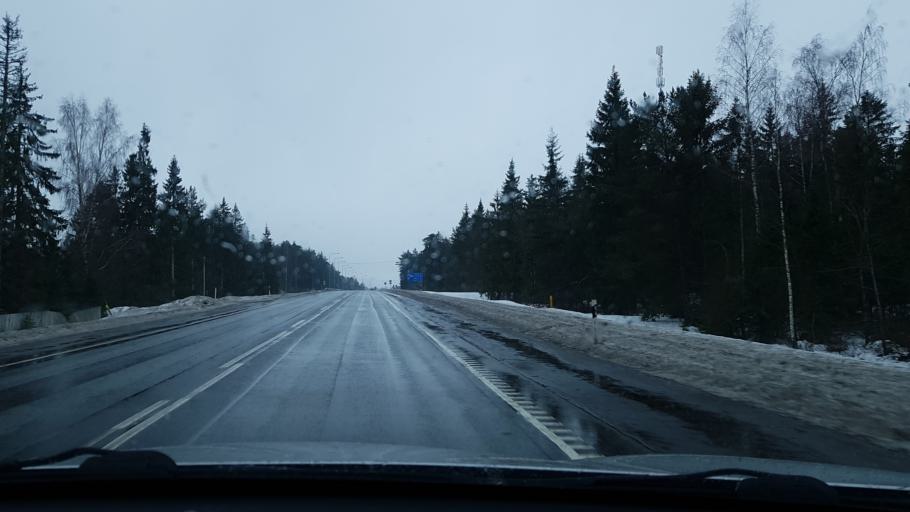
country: EE
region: Raplamaa
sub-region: Kohila vald
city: Kohila
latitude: 59.1856
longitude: 24.7854
